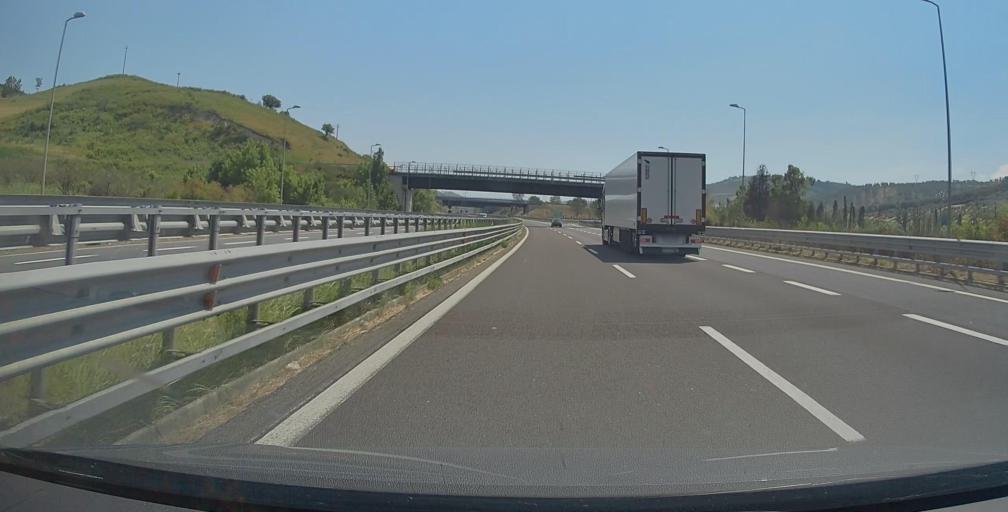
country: IT
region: Calabria
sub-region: Provincia di Vibo-Valentia
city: San Gregorio d'Ippona
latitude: 38.6277
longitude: 16.1624
